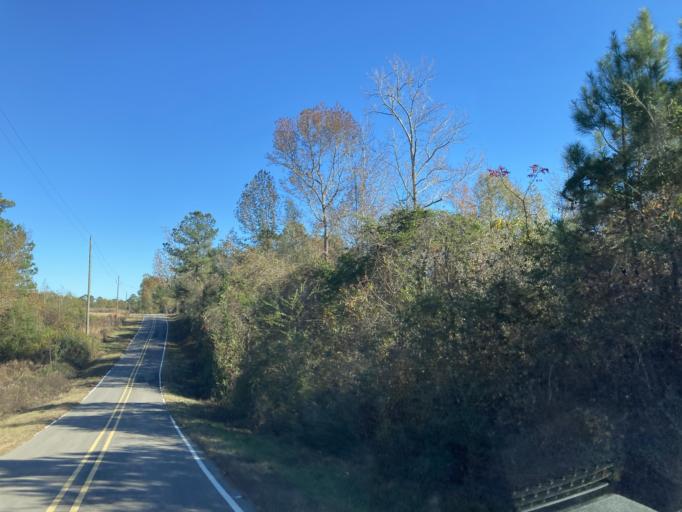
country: US
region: Mississippi
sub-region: Lamar County
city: Sumrall
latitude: 31.3356
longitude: -89.6210
